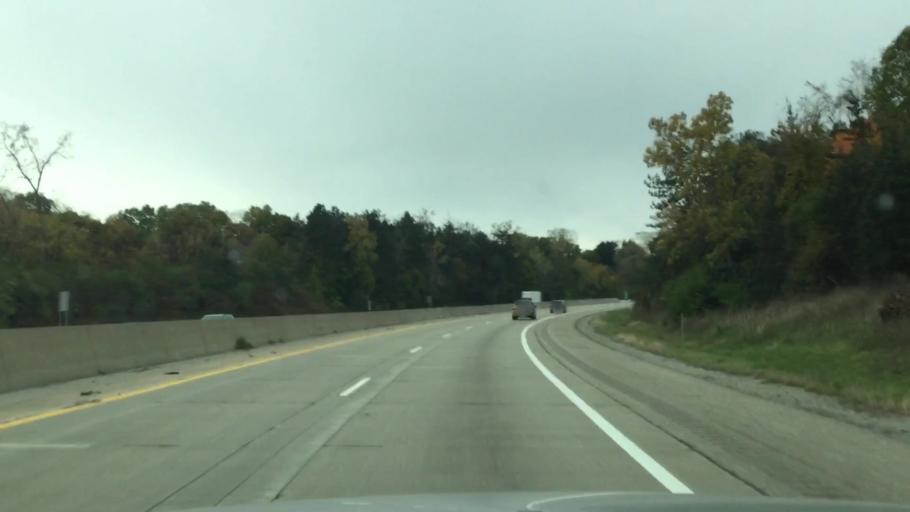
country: US
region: Michigan
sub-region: Washtenaw County
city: Ann Arbor
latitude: 42.2989
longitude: -83.7497
